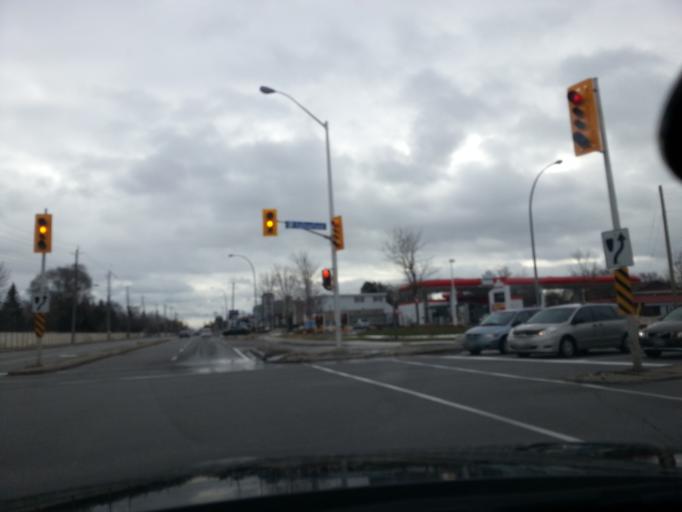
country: CA
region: Ontario
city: Bells Corners
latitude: 45.2883
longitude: -75.7572
